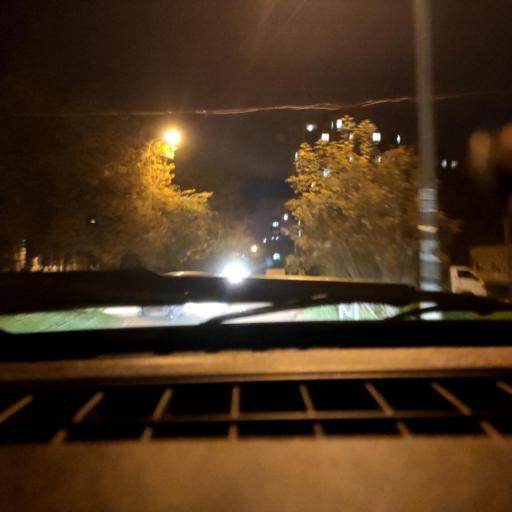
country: RU
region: Bashkortostan
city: Ufa
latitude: 54.7590
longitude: 56.0025
